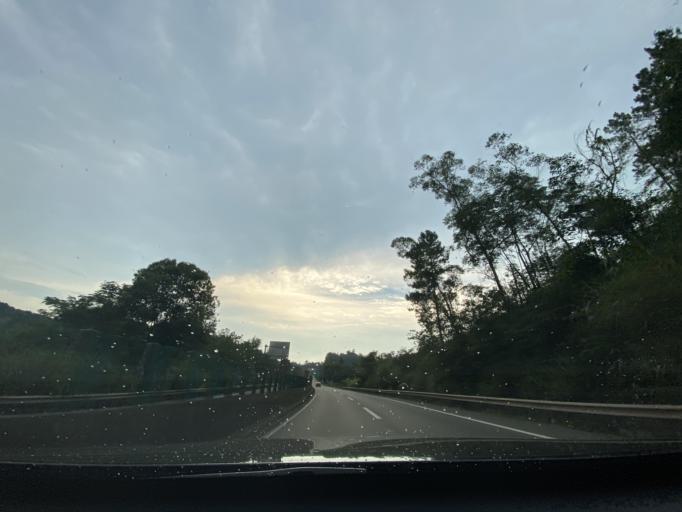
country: CN
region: Sichuan
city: Chonglong
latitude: 29.7981
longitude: 104.7212
